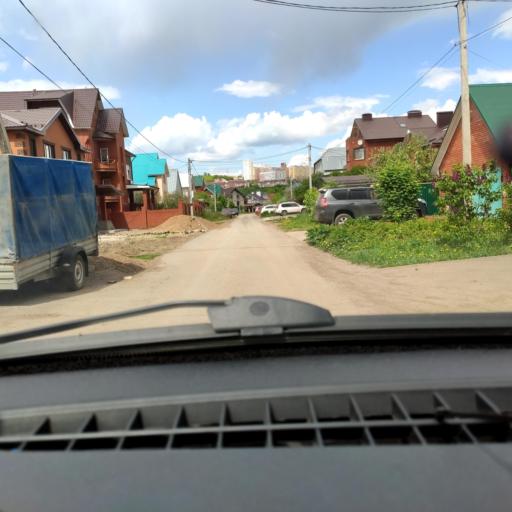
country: RU
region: Bashkortostan
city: Ufa
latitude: 54.6867
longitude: 55.9767
